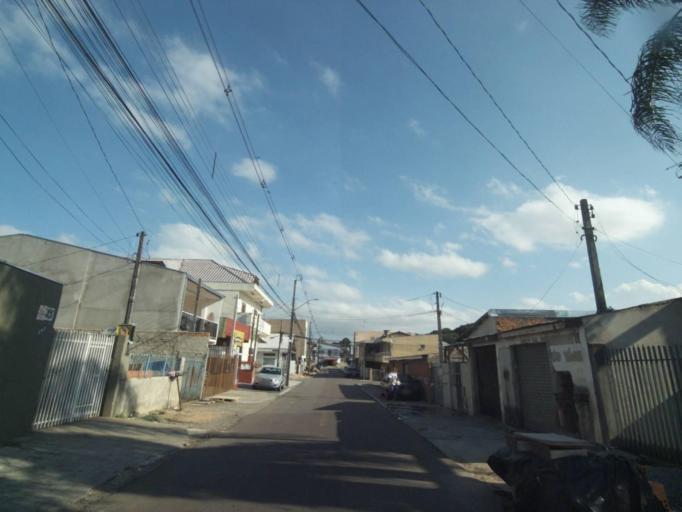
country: BR
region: Parana
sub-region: Araucaria
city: Araucaria
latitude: -25.5304
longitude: -49.3332
